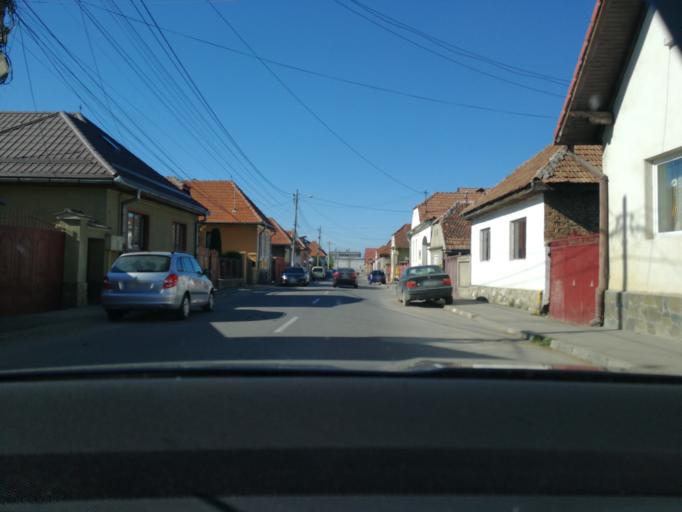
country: RO
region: Brasov
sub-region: Oras Rasnov
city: Rasnov
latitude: 45.5875
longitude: 25.4585
